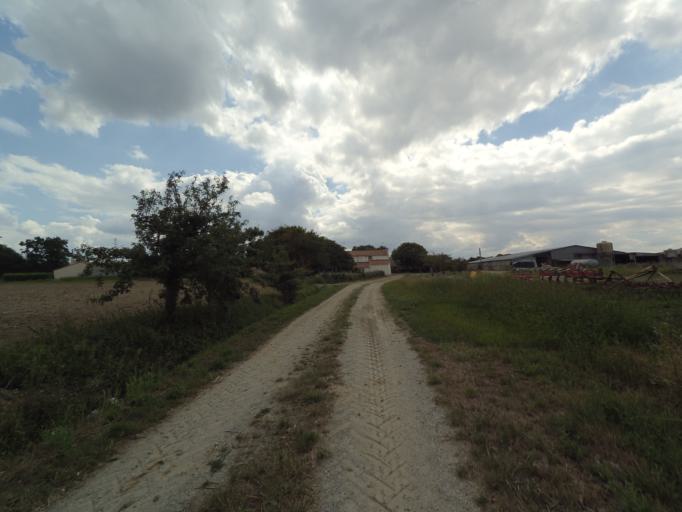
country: FR
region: Pays de la Loire
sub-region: Departement de la Loire-Atlantique
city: Vieillevigne
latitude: 46.9758
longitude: -1.4182
